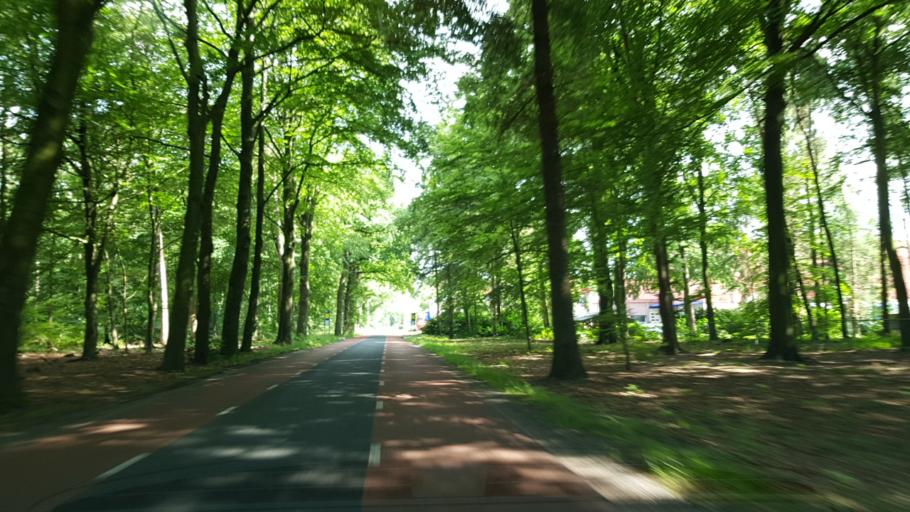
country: NL
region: Gelderland
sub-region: Gemeente Apeldoorn
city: Uddel
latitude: 52.2871
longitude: 5.7300
